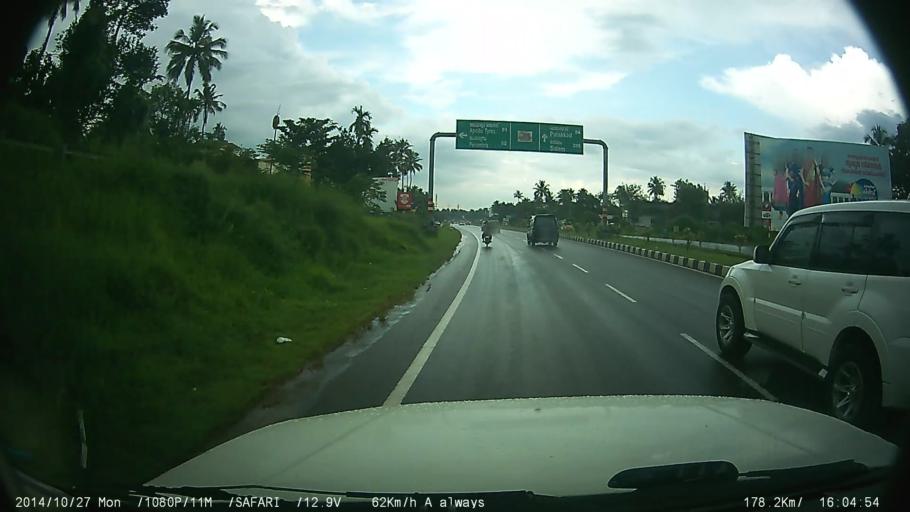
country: IN
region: Kerala
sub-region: Thrissur District
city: Kizhake Chalakudi
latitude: 10.3416
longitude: 76.3222
